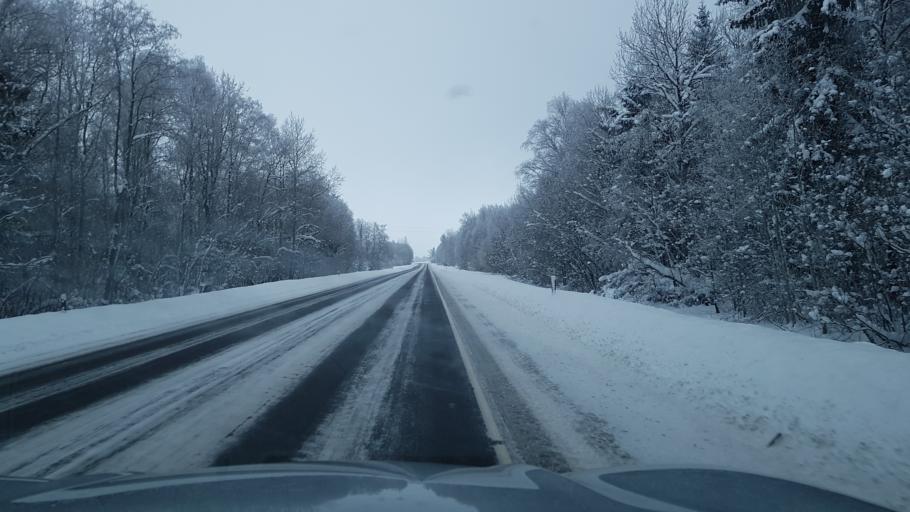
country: EE
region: Ida-Virumaa
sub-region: Johvi vald
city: Johvi
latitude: 59.2782
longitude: 27.3913
